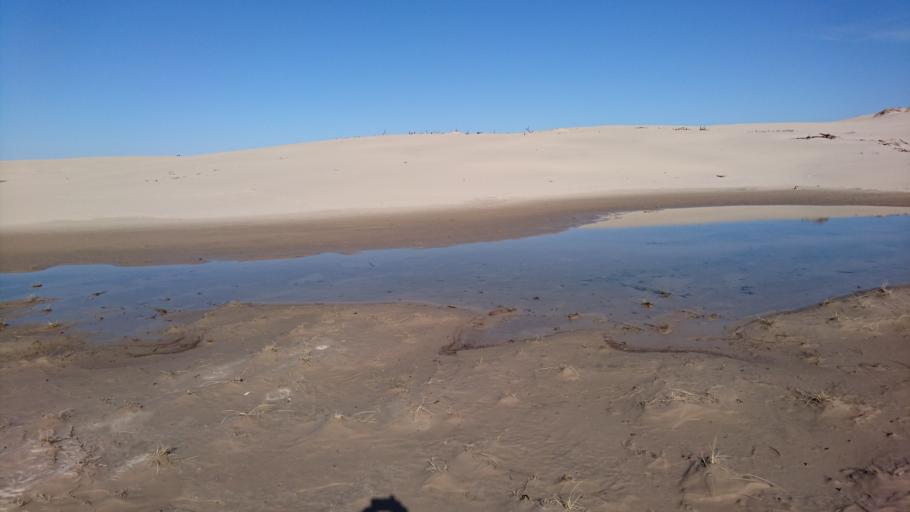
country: DK
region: North Denmark
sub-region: Frederikshavn Kommune
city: Strandby
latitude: 57.6475
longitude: 10.4044
